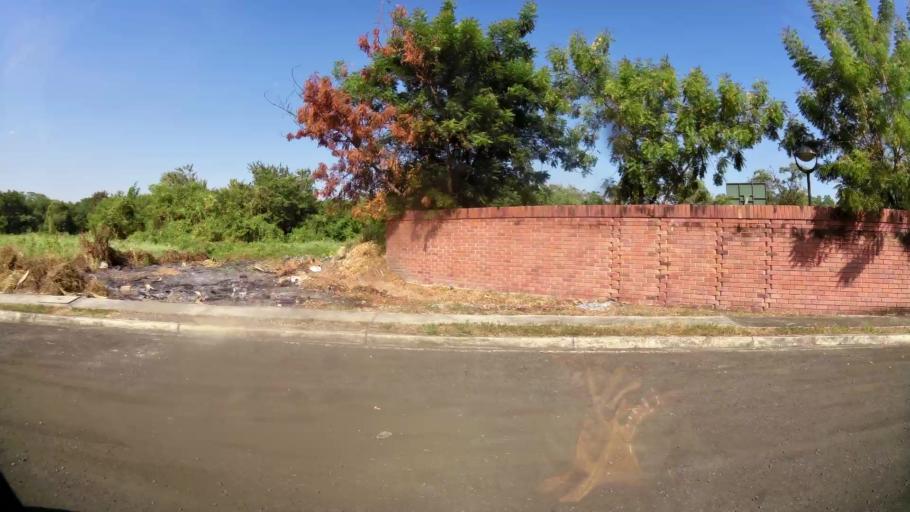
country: EC
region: Guayas
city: Santa Lucia
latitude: -2.1926
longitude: -79.9986
